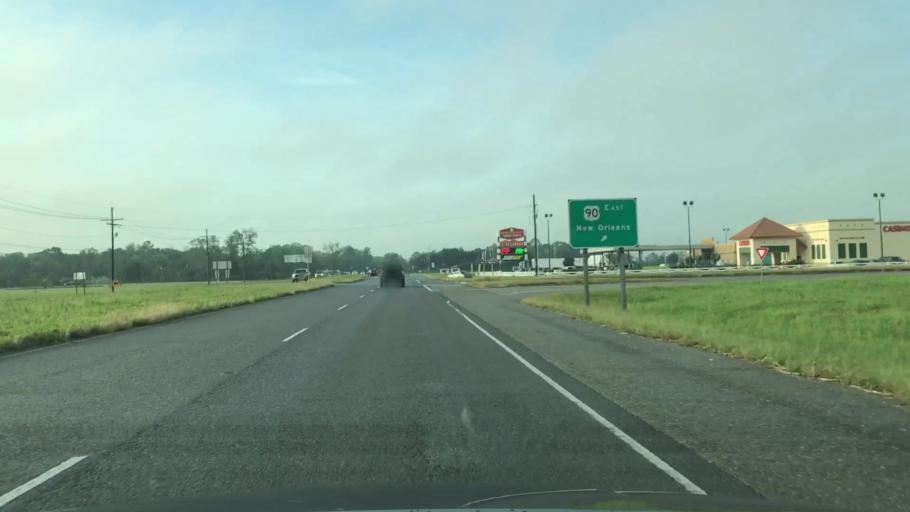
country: US
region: Louisiana
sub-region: Terrebonne Parish
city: Gray
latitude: 29.6802
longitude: -90.8123
